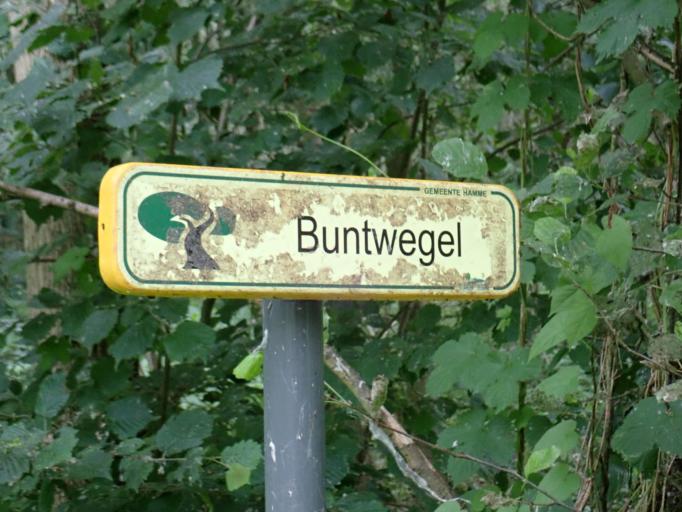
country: BE
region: Flanders
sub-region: Provincie Oost-Vlaanderen
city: Hamme
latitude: 51.1038
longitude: 4.1571
